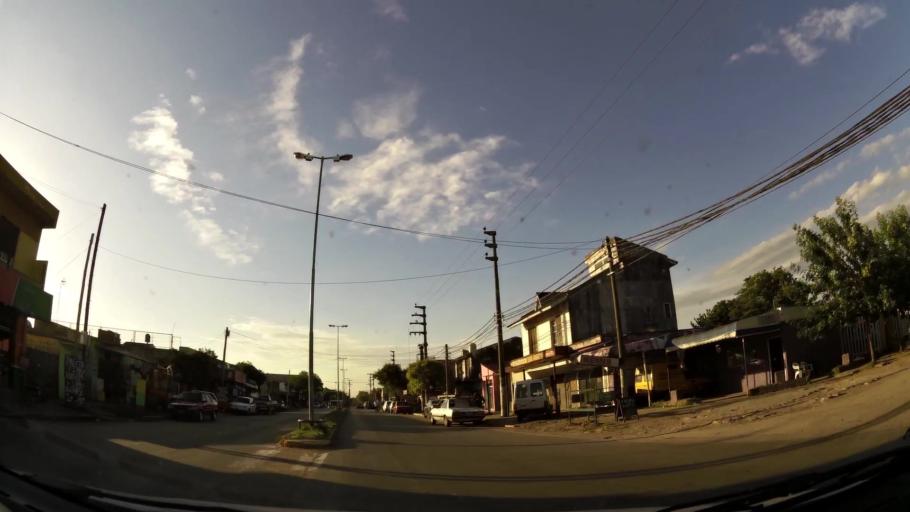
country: AR
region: Buenos Aires
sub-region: Partido de Merlo
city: Merlo
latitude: -34.6974
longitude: -58.7520
